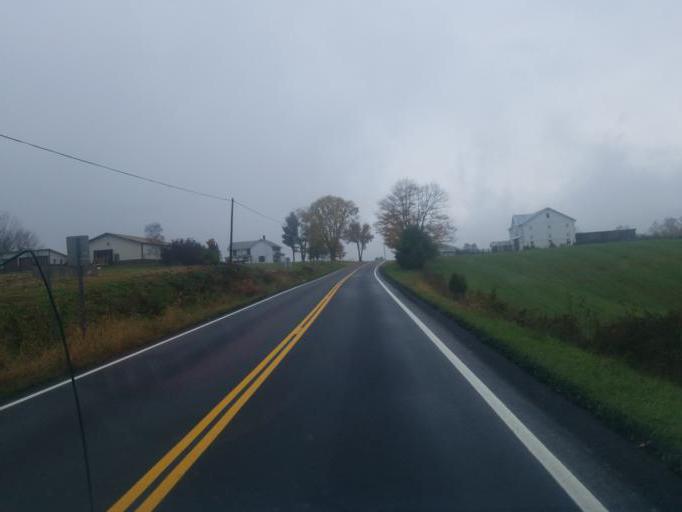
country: US
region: Ohio
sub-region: Morgan County
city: McConnelsville
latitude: 39.5491
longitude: -81.8214
